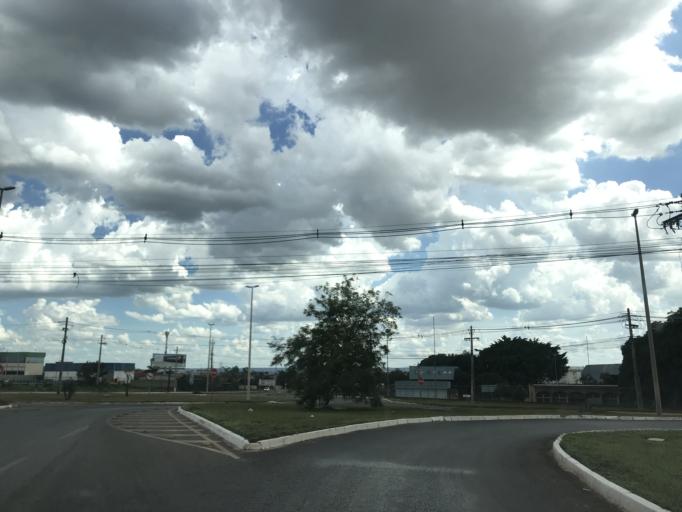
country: BR
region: Federal District
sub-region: Brasilia
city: Brasilia
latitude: -15.7966
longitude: -47.9717
